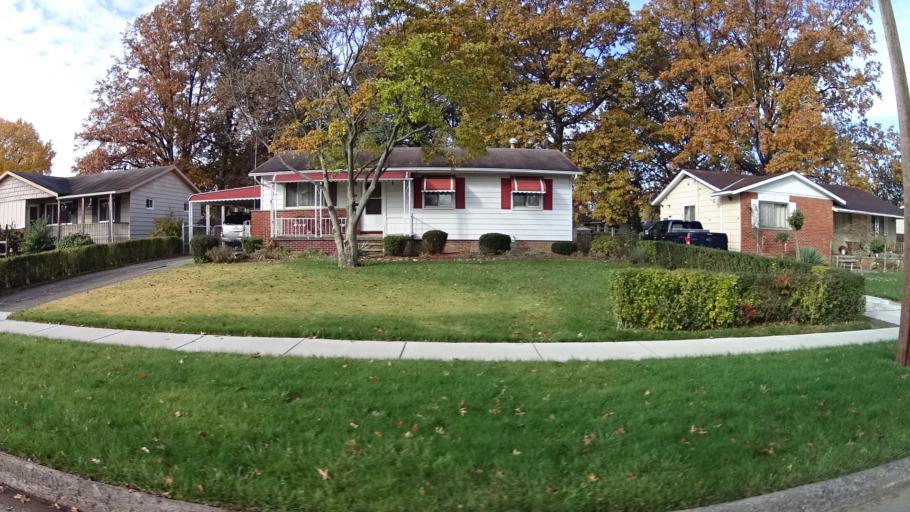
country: US
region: Ohio
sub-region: Lorain County
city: Sheffield
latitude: 41.4342
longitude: -82.1258
